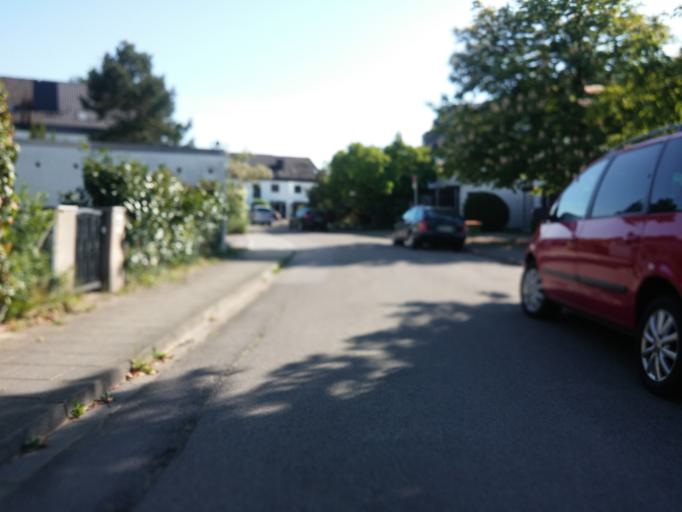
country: DE
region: Bavaria
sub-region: Upper Bavaria
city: Vaterstetten
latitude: 48.0943
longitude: 11.7693
